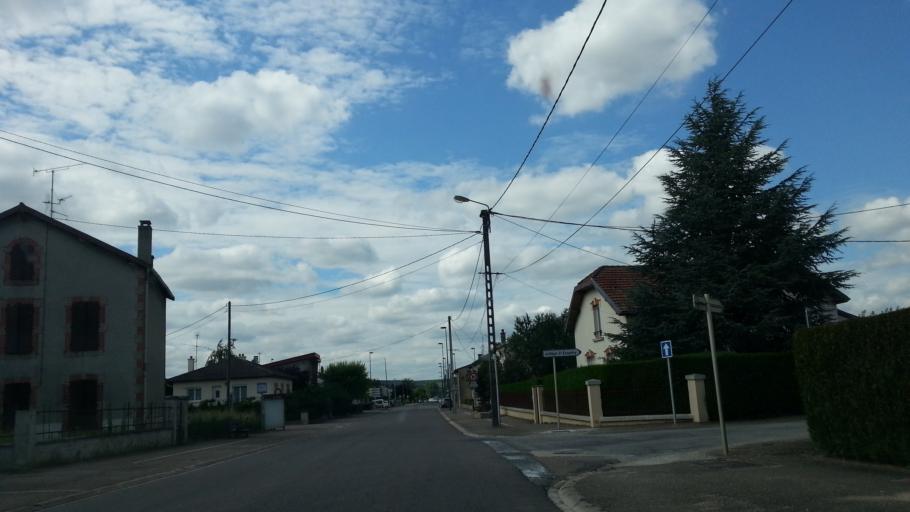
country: FR
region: Lorraine
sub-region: Departement de la Meuse
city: Thierville-sur-Meuse
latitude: 49.1690
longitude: 5.3531
